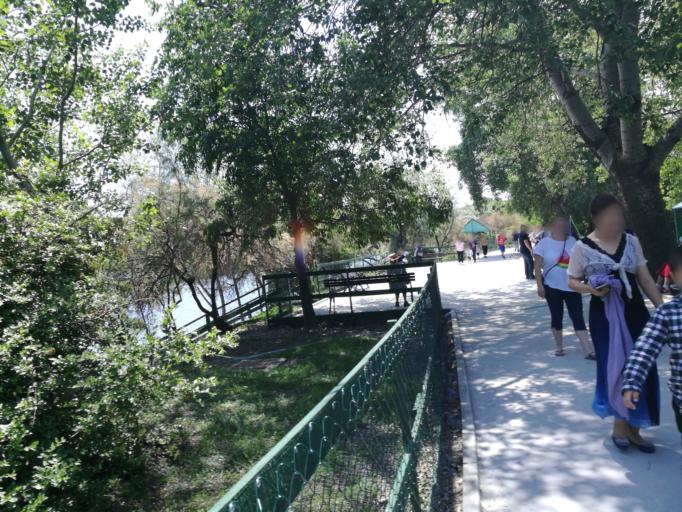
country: RO
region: Constanta
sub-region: Municipiul Constanta
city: Constanta
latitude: 44.2057
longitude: 28.6406
